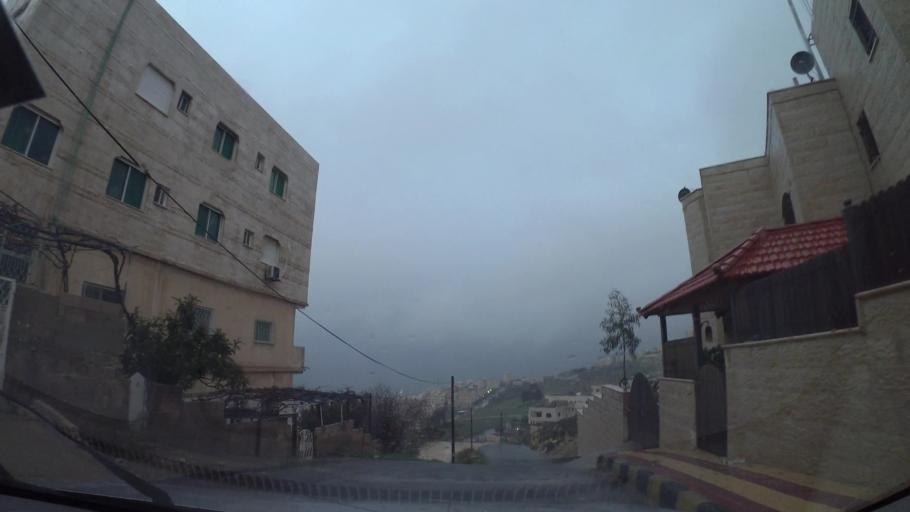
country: JO
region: Amman
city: Al Jubayhah
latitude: 32.0276
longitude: 35.8424
